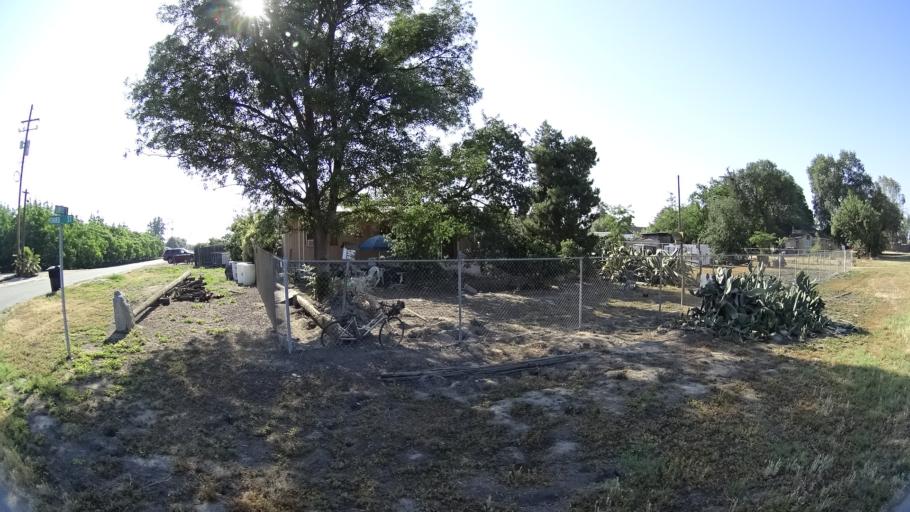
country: US
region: California
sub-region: Fresno County
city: Laton
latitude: 36.4031
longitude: -119.7214
